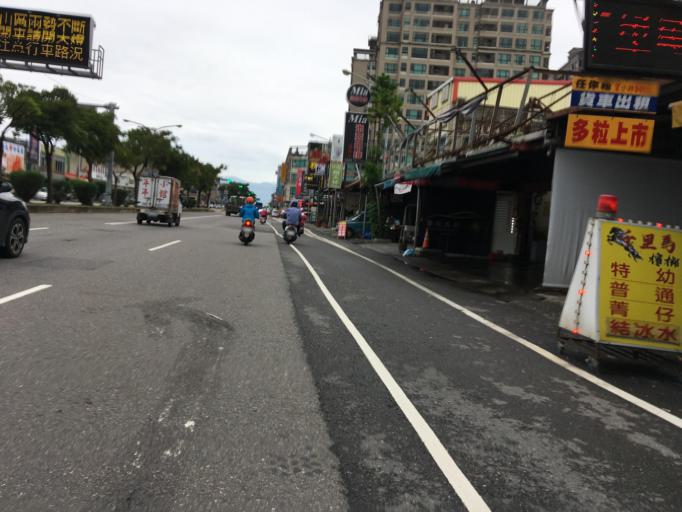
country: TW
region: Taiwan
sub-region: Yilan
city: Yilan
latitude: 24.6891
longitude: 121.7706
